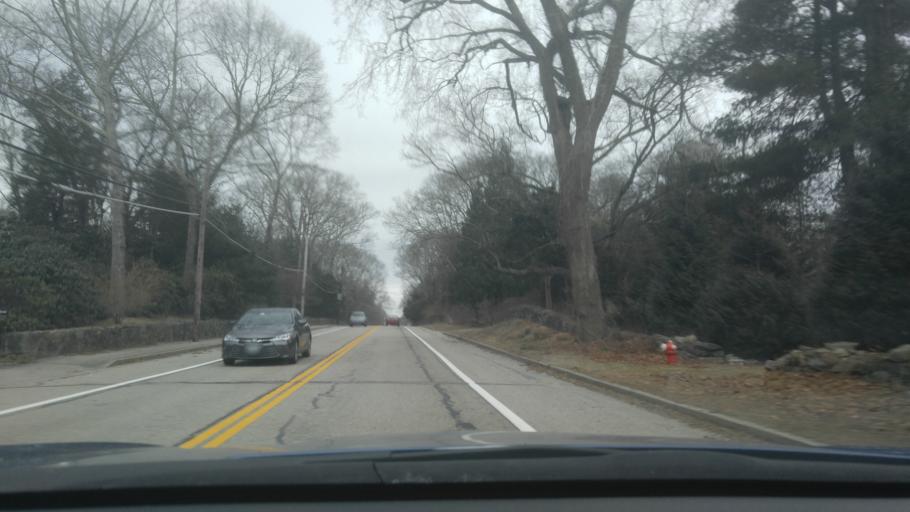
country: US
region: Rhode Island
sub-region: Washington County
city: North Kingstown
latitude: 41.5637
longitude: -71.4473
